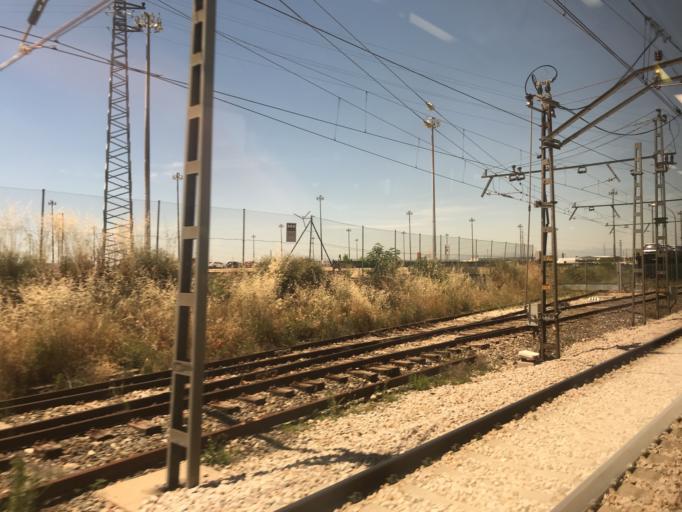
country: ES
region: Madrid
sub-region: Provincia de Madrid
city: Pinto
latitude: 40.2550
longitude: -3.7042
